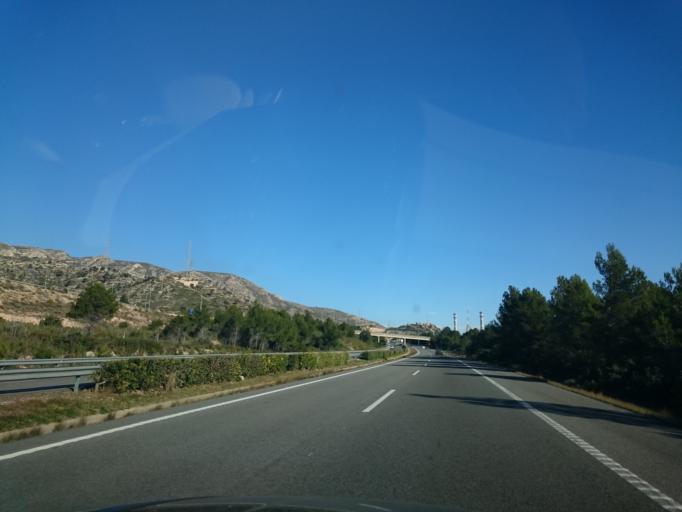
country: ES
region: Catalonia
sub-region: Provincia de Tarragona
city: l'Ametlla de Mar
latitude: 40.9496
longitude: 0.8603
